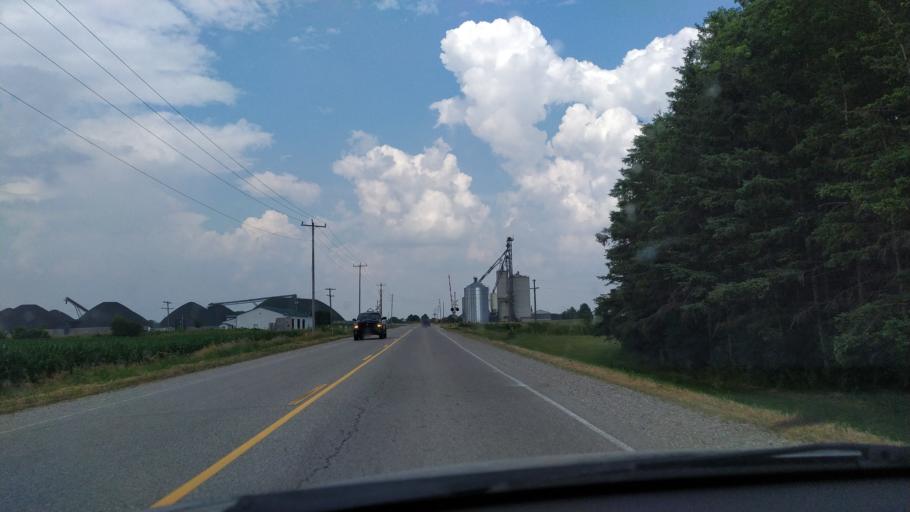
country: CA
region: Ontario
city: Dorchester
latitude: 43.1654
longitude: -81.1421
